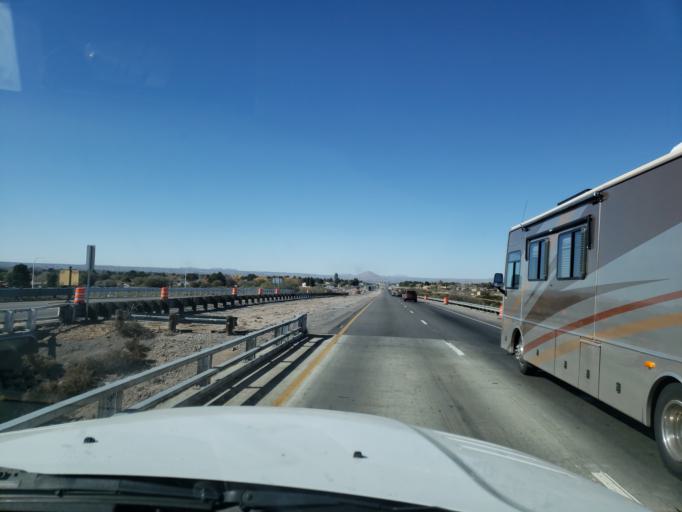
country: US
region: New Mexico
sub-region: Dona Ana County
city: University Park
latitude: 32.2655
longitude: -106.7385
